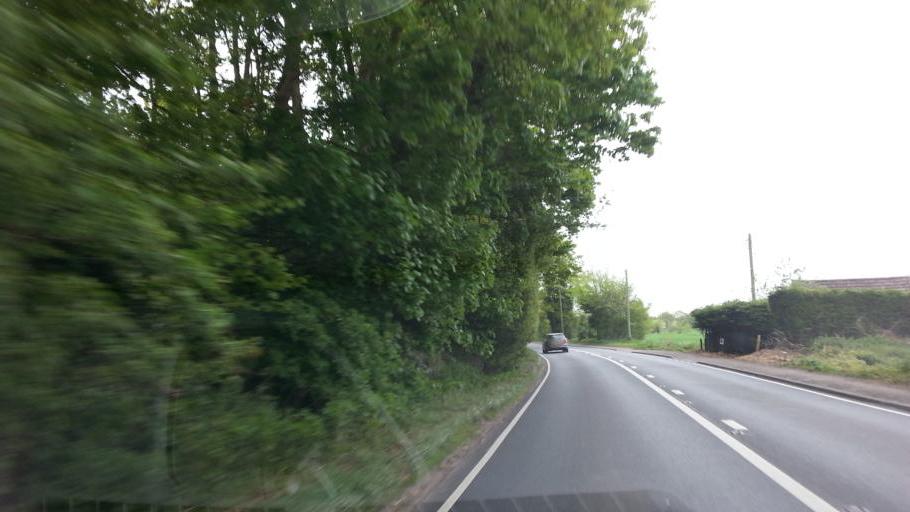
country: GB
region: England
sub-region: Suffolk
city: Bury St Edmunds
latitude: 52.2177
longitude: 0.7431
